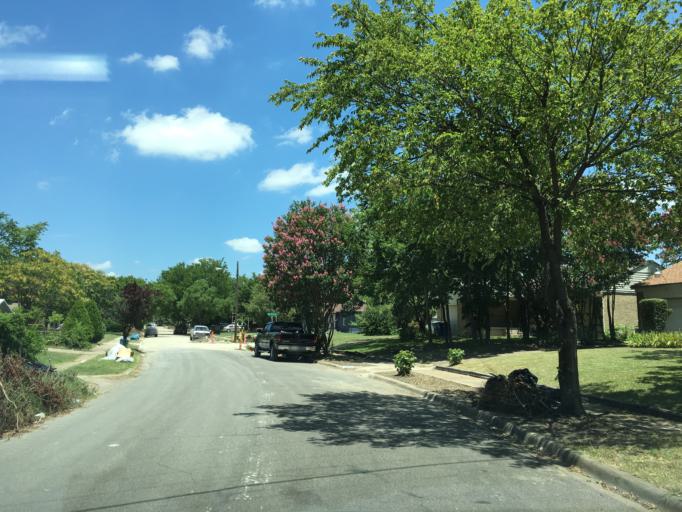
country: US
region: Texas
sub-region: Dallas County
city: Garland
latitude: 32.8429
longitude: -96.6722
